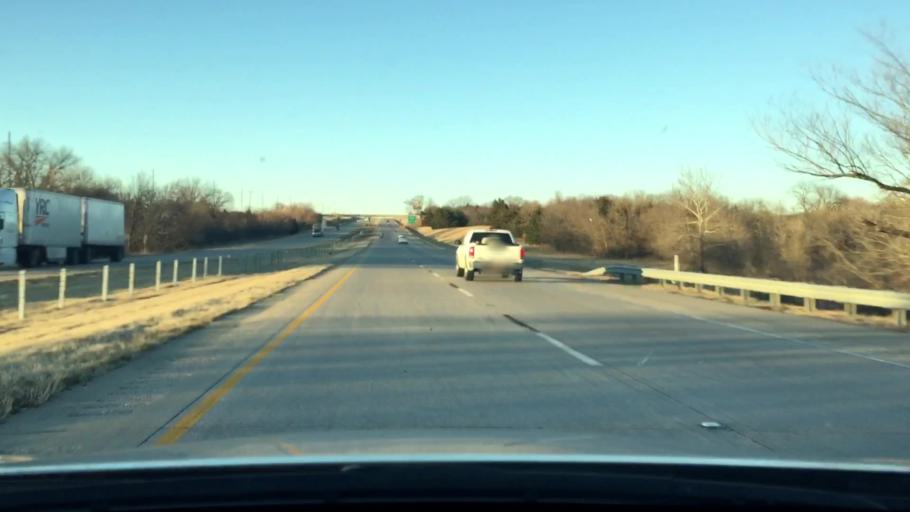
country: US
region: Oklahoma
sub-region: Love County
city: Marietta
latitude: 33.8779
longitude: -97.1342
